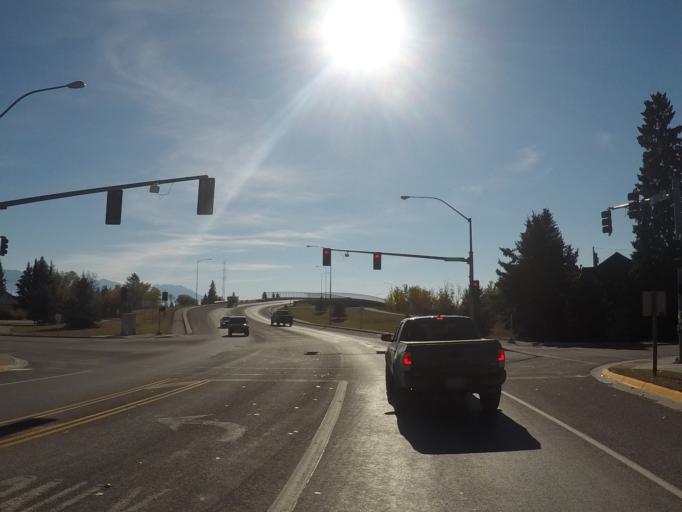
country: US
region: Montana
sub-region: Flathead County
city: Whitefish
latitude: 48.4160
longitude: -114.3409
